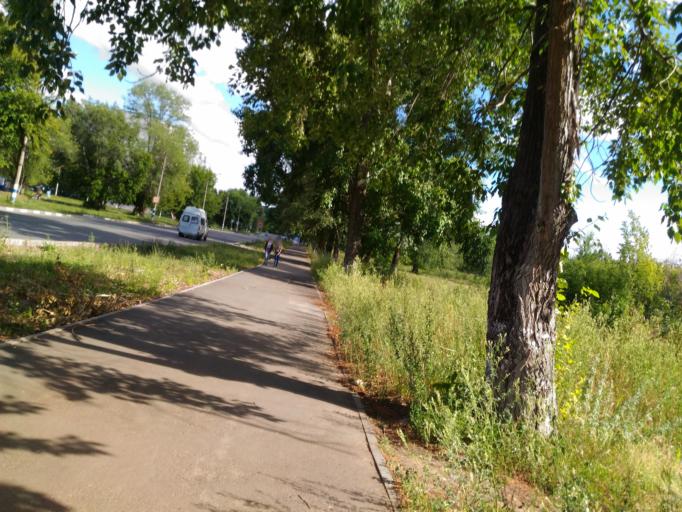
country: RU
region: Ulyanovsk
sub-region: Ulyanovskiy Rayon
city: Ulyanovsk
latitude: 54.3256
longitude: 48.4808
